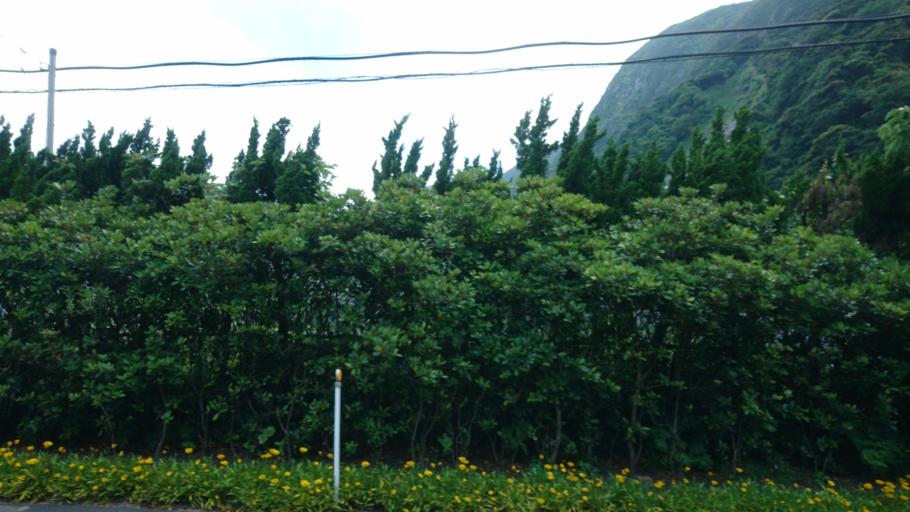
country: JP
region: Shizuoka
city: Shimoda
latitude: 34.4109
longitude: 139.2766
